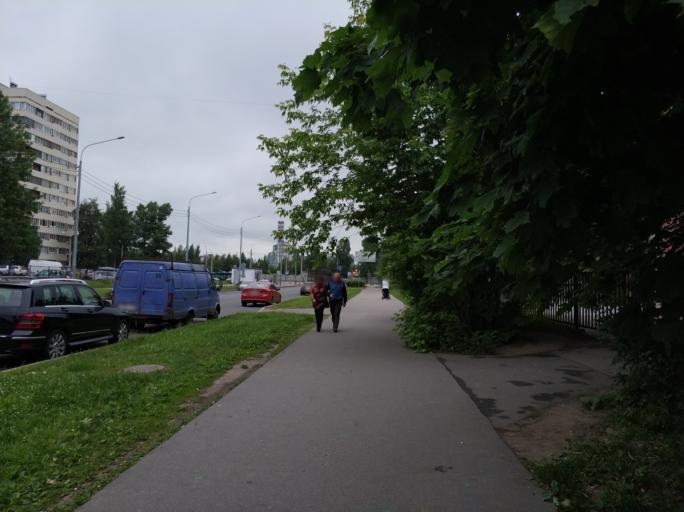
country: RU
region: St.-Petersburg
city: Grazhdanka
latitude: 60.0436
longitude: 30.4168
